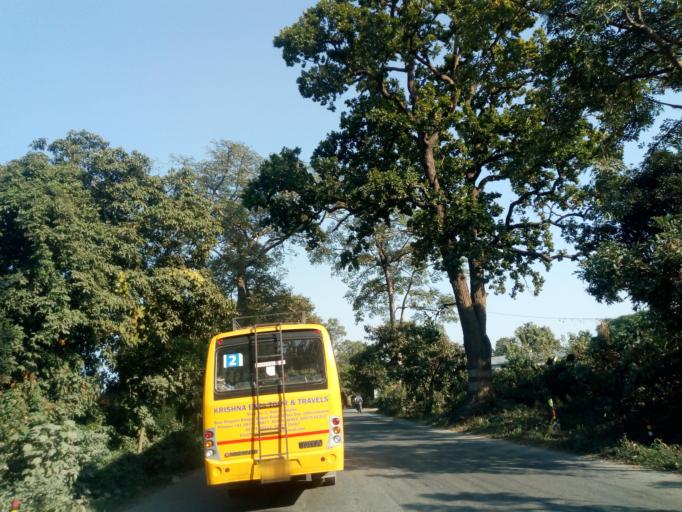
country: IN
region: Uttarakhand
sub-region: Dehradun
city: Dehradun
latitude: 30.3496
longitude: 77.8865
